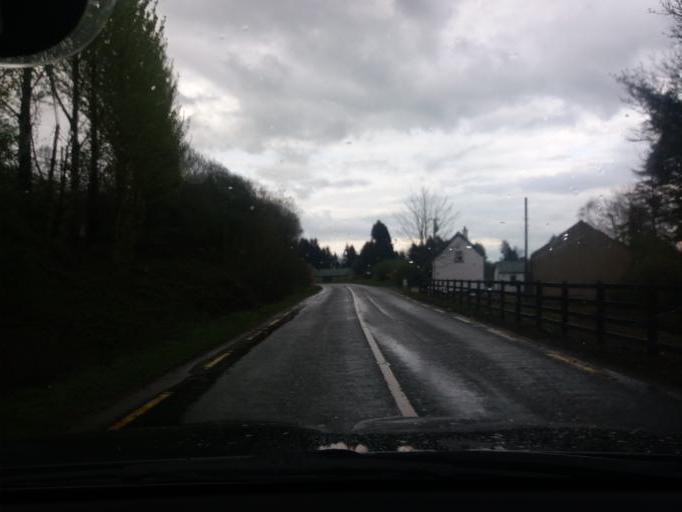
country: IE
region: Ulster
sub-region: An Cabhan
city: Ballyconnell
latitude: 54.1159
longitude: -7.6606
